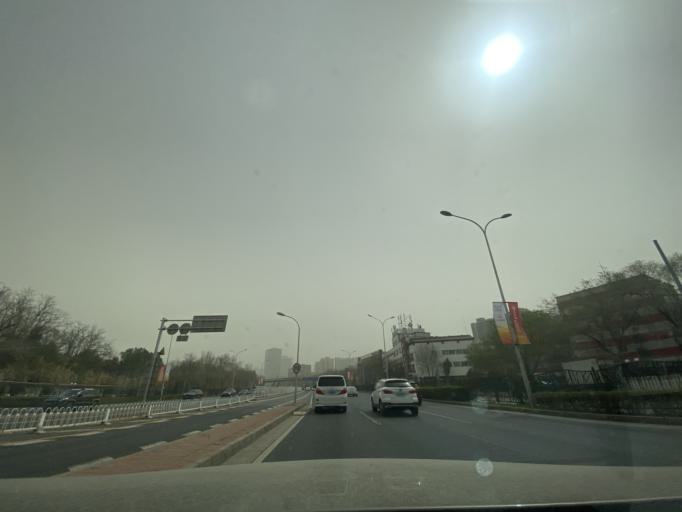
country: CN
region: Beijing
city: Sijiqing
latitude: 39.9390
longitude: 116.3091
